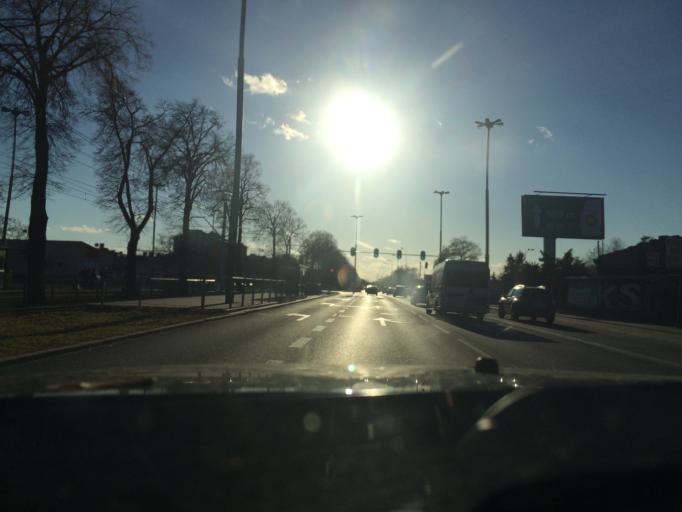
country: PL
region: Lodz Voivodeship
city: Lodz
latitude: 51.7235
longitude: 19.4431
